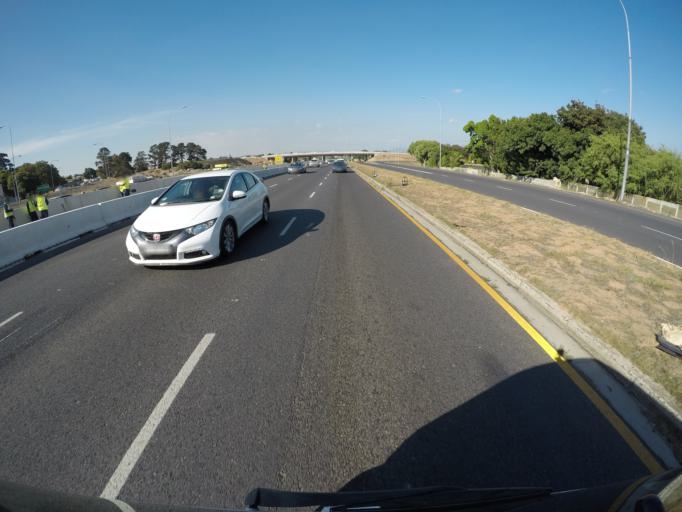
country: ZA
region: Western Cape
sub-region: City of Cape Town
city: Kraaifontein
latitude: -33.8781
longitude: 18.6564
